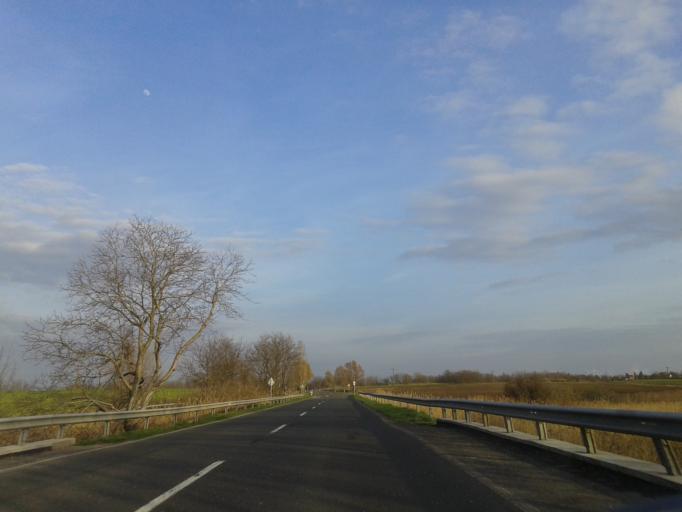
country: HU
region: Komarom-Esztergom
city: Acs
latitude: 47.7244
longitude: 18.0137
